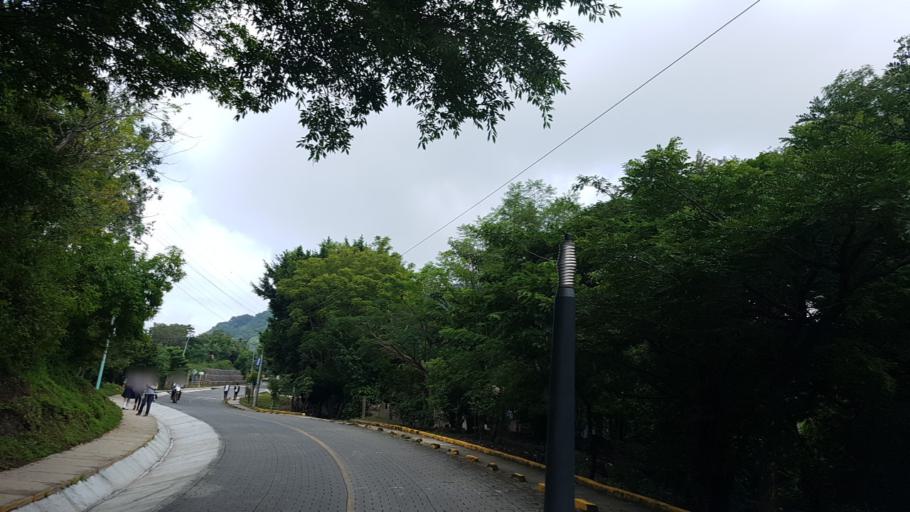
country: NI
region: Leon
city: Santa Rosa del Penon
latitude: 12.9314
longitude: -86.3450
